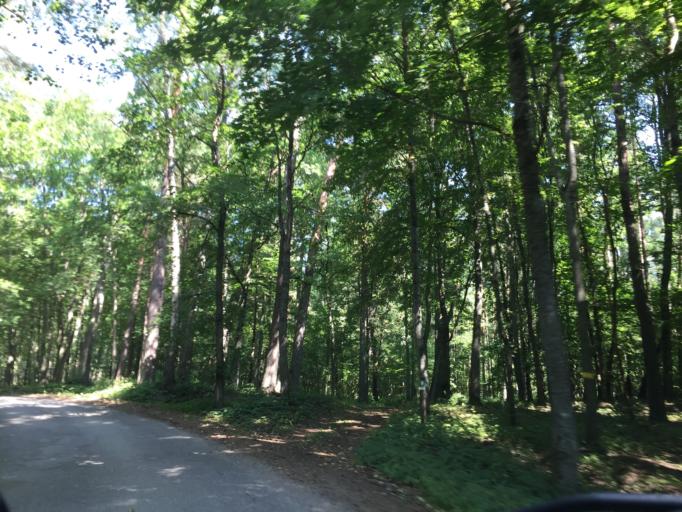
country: LV
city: Tervete
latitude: 56.4816
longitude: 23.3978
